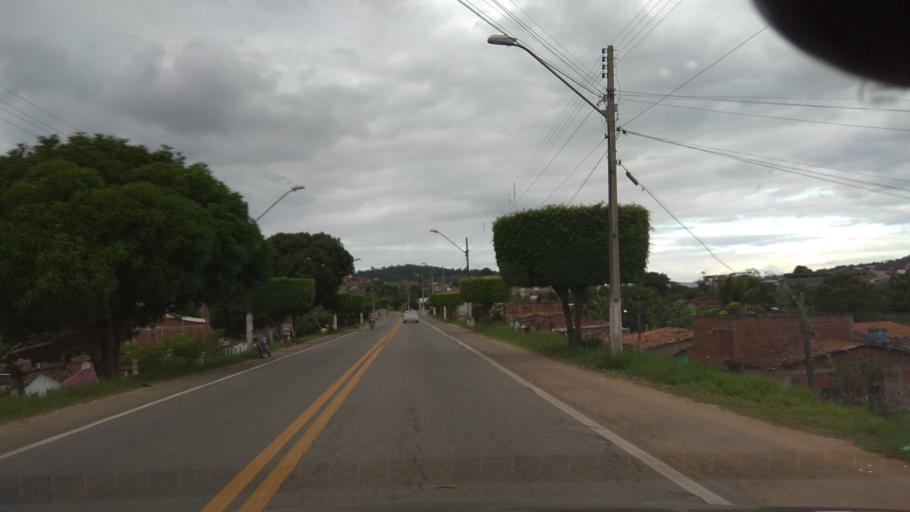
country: BR
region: Bahia
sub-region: Ubata
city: Ubata
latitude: -14.2097
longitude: -39.5251
